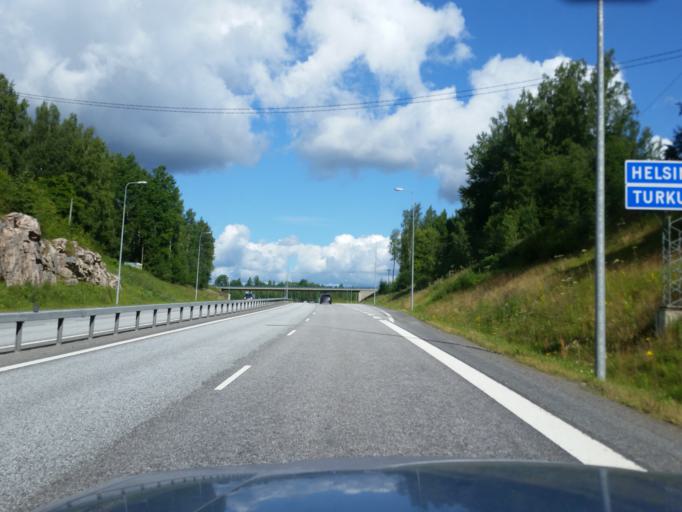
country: FI
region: Uusimaa
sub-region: Helsinki
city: Vihti
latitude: 60.2995
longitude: 24.3591
